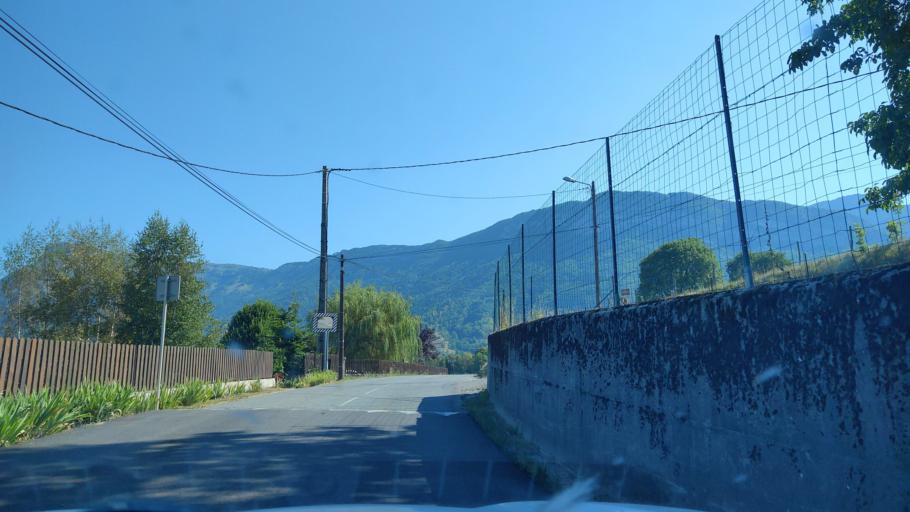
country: FR
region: Rhone-Alpes
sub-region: Departement de la Savoie
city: Barby
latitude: 45.5713
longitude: 6.0265
